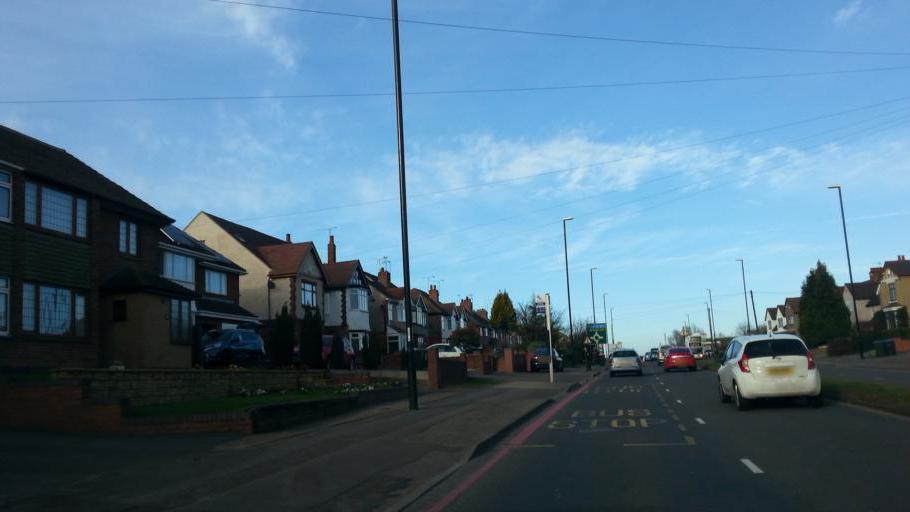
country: GB
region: England
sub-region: Warwickshire
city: Exhall
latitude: 52.4280
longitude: -1.4409
